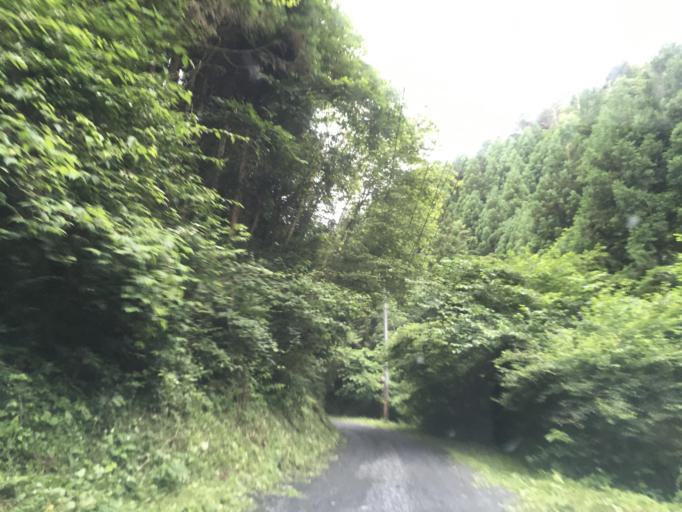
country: JP
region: Iwate
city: Ichinoseki
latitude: 38.7782
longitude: 141.4200
